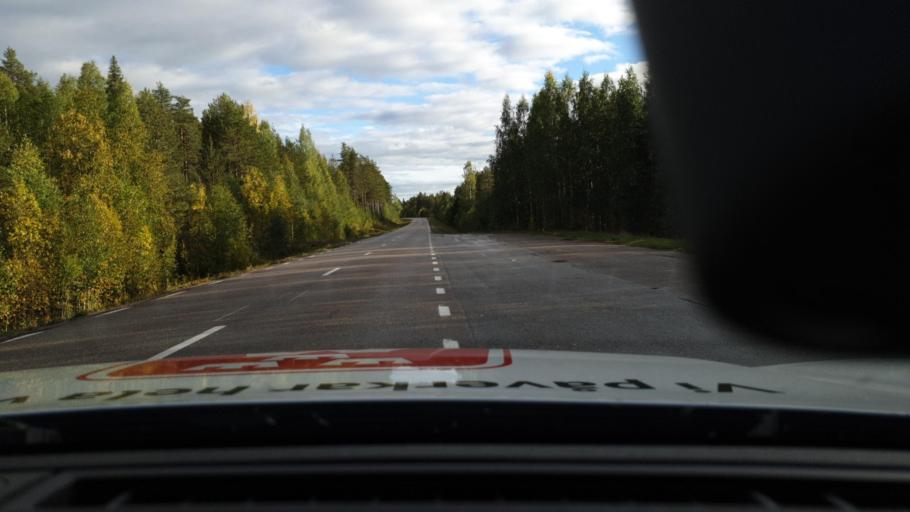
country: SE
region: Norrbotten
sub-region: Overkalix Kommun
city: OEverkalix
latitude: 66.6464
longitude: 22.7208
